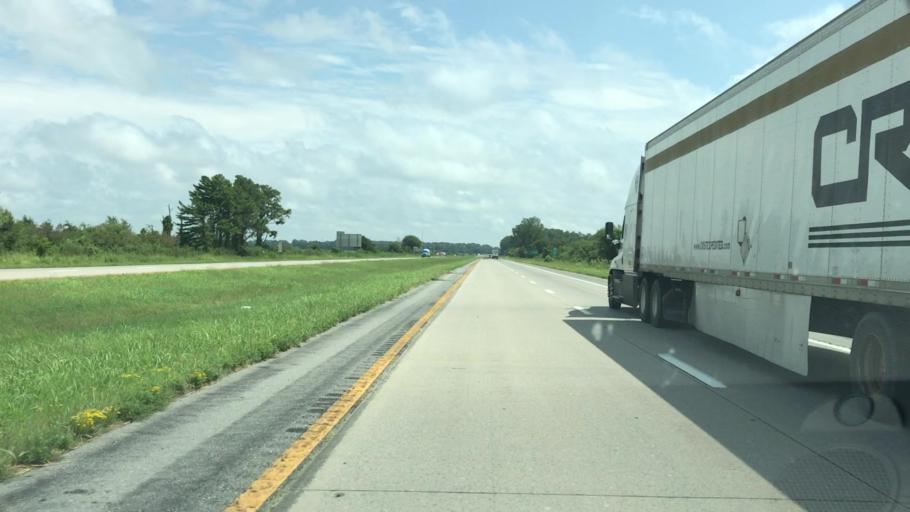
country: US
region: Missouri
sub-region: Pemiscot County
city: Caruthersville
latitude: 36.1466
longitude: -89.6524
